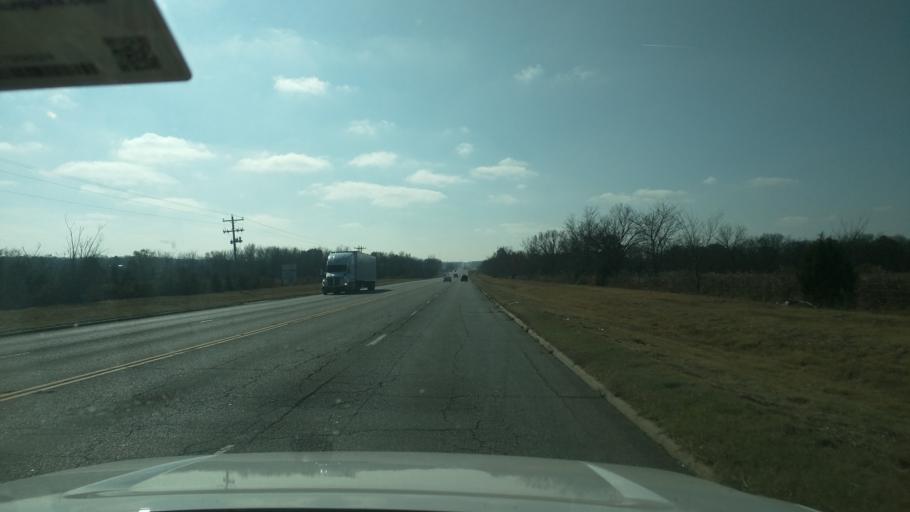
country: US
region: Oklahoma
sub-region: Washington County
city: Bartlesville
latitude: 36.6768
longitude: -95.9353
